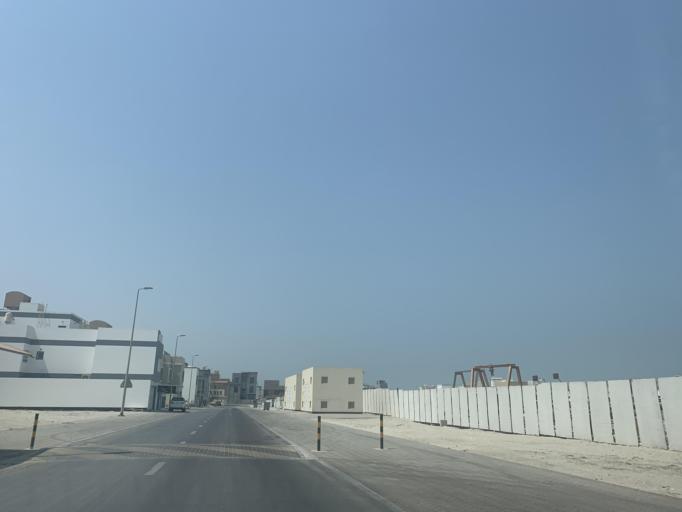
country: BH
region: Muharraq
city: Al Hadd
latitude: 26.2372
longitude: 50.6594
